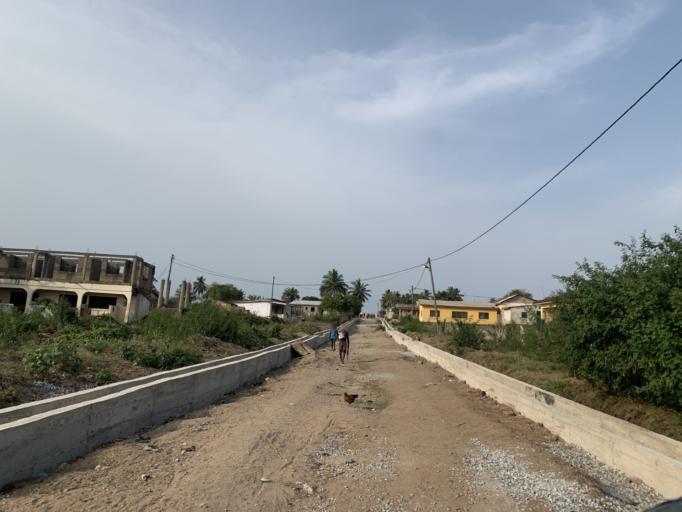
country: GH
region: Central
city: Winneba
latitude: 5.3342
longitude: -0.6247
